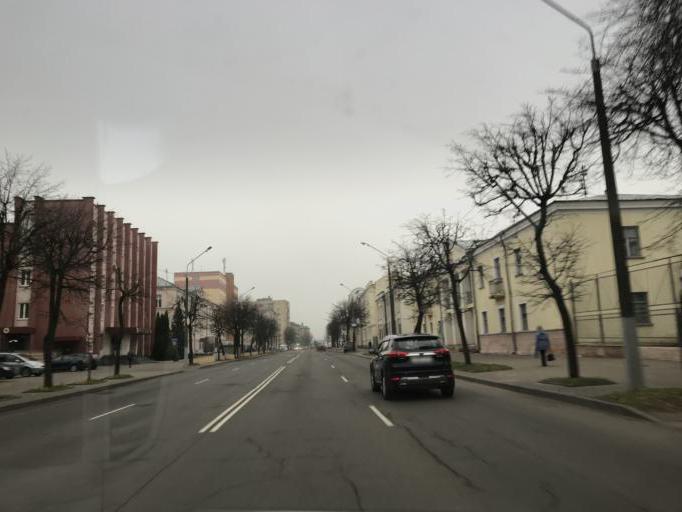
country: BY
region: Mogilev
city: Mahilyow
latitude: 53.9001
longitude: 30.3412
